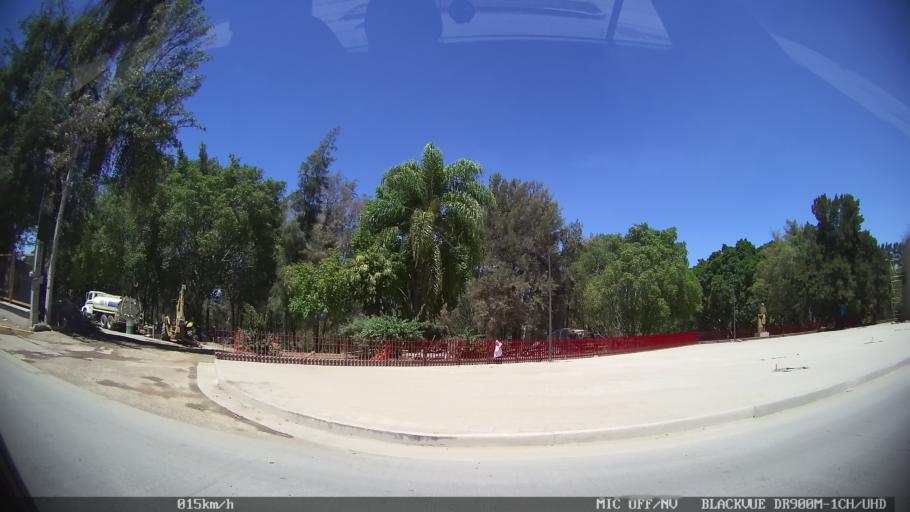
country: MX
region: Jalisco
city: Tlaquepaque
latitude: 20.6713
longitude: -103.2700
